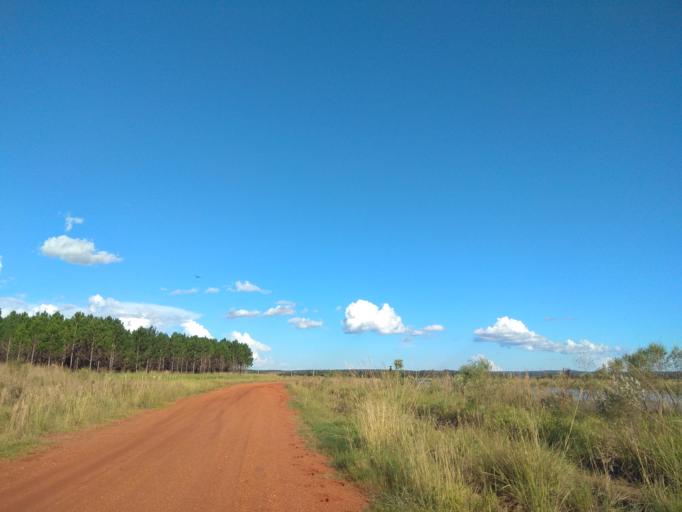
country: AR
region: Misiones
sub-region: Departamento de Candelaria
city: Candelaria
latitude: -27.4922
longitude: -55.7765
